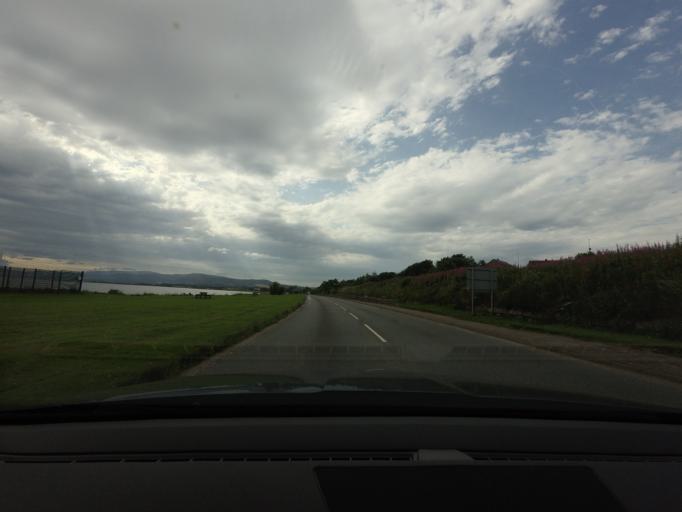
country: GB
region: Scotland
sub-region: Highland
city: Invergordon
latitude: 57.6890
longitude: -4.1792
